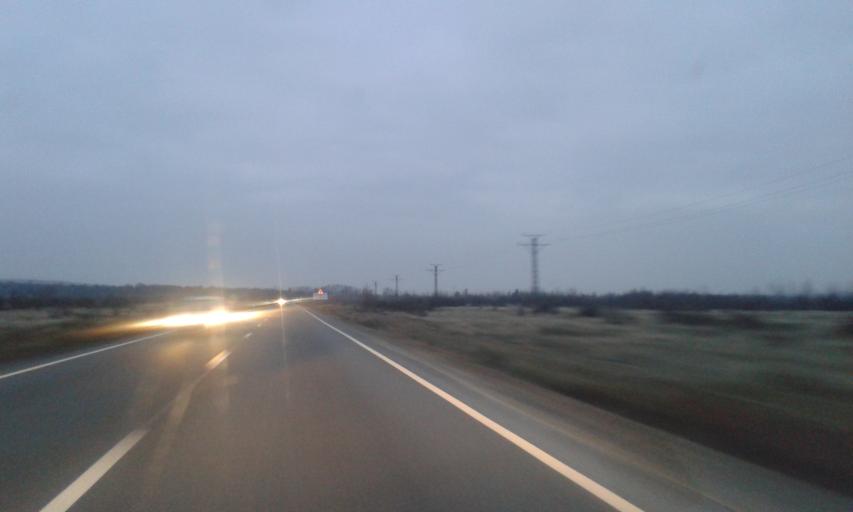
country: RO
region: Gorj
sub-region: Comuna Bumbesti-Jiu
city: Bumbesti-Jiu
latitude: 45.1383
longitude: 23.3675
